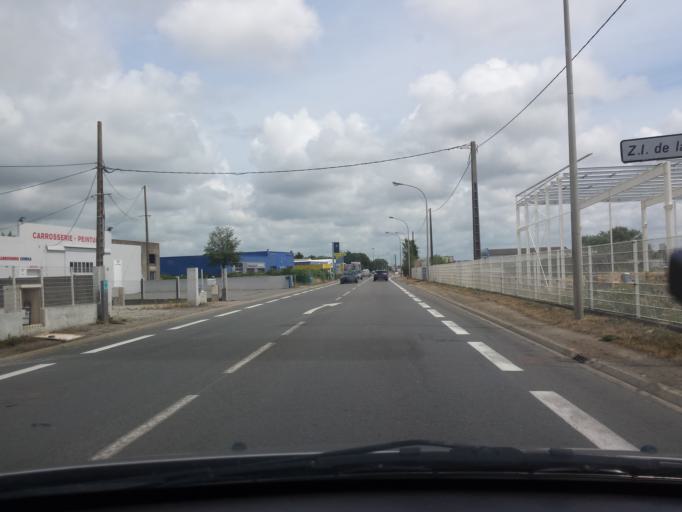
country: FR
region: Pays de la Loire
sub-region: Departement de la Vendee
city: Le Fenouiller
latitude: 46.6938
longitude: -1.9040
